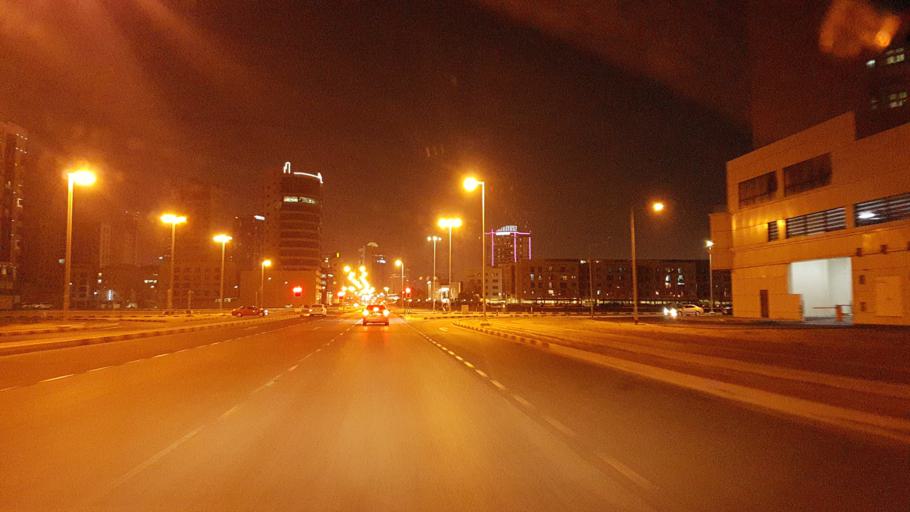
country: BH
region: Manama
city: Jidd Hafs
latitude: 26.2366
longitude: 50.5280
